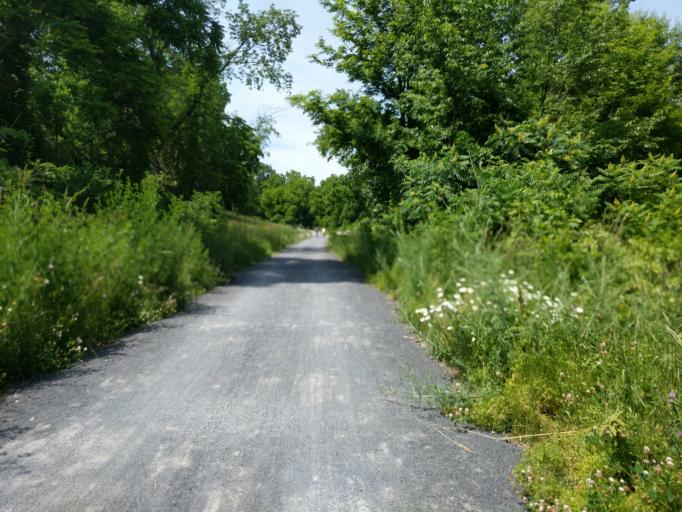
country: US
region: New York
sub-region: Tompkins County
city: Northwest Ithaca
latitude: 42.4978
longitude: -76.5446
